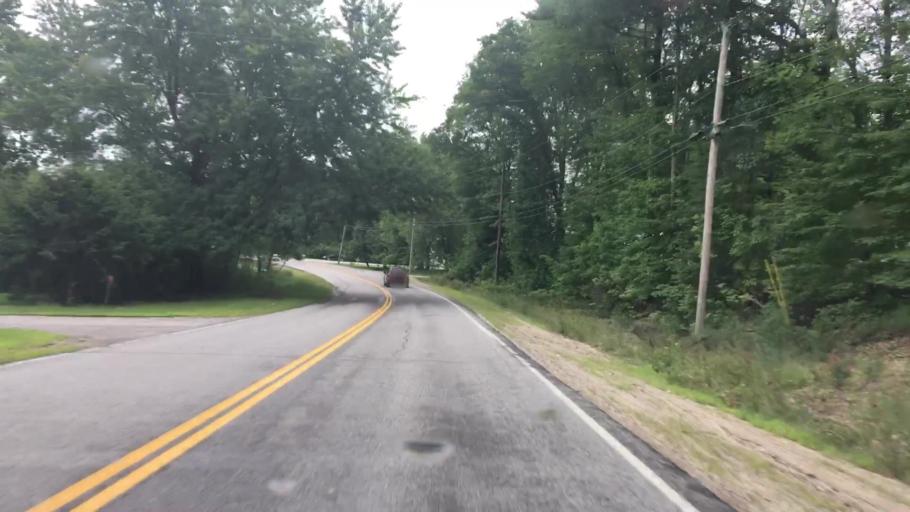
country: US
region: Maine
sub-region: Oxford County
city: Brownfield
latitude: 43.9530
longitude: -70.8957
